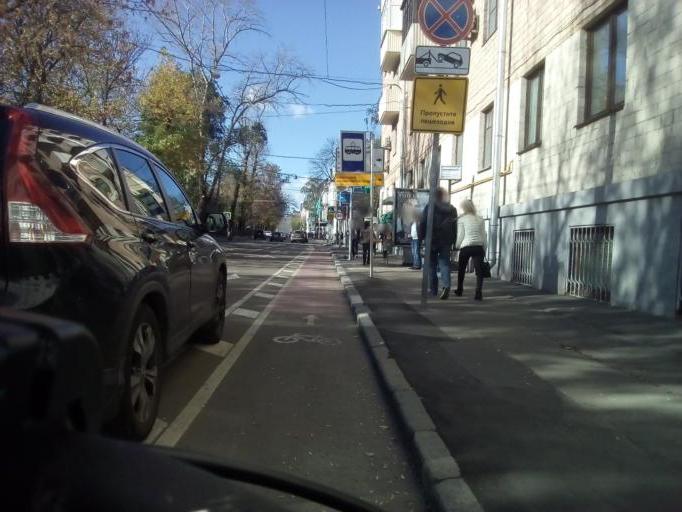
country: RU
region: Moscow
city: Moscow
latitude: 55.7630
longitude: 37.6430
